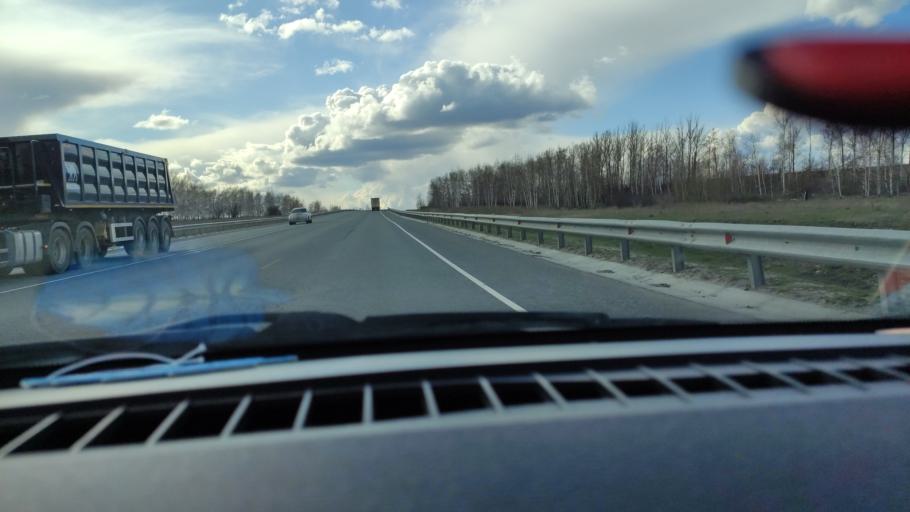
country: RU
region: Saratov
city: Shikhany
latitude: 52.1209
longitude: 47.2627
